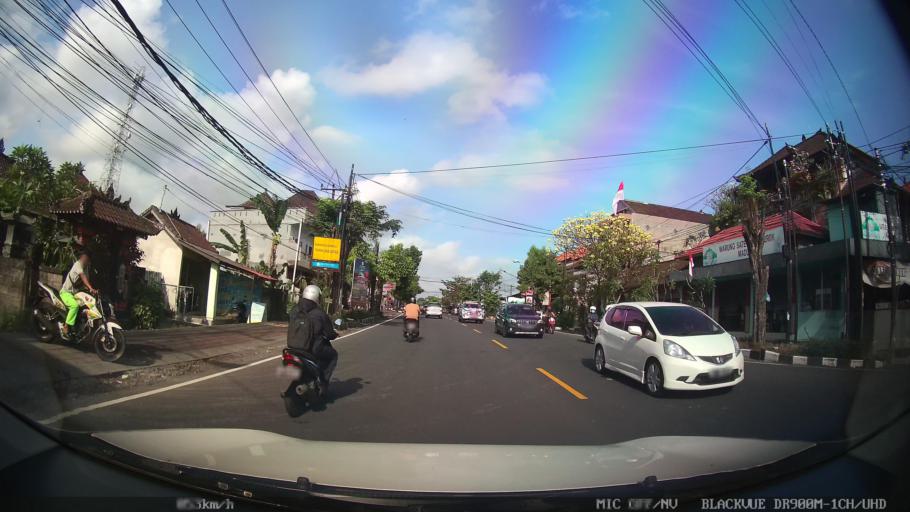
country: ID
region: Bali
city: Banjar Jumbayah
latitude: -8.5631
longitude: 115.1655
